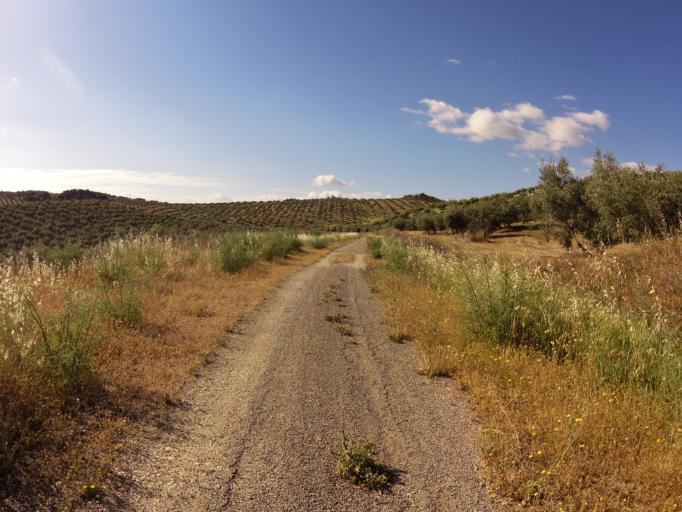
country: ES
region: Andalusia
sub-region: Province of Cordoba
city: Fuente-Tojar
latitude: 37.5816
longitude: -4.1856
